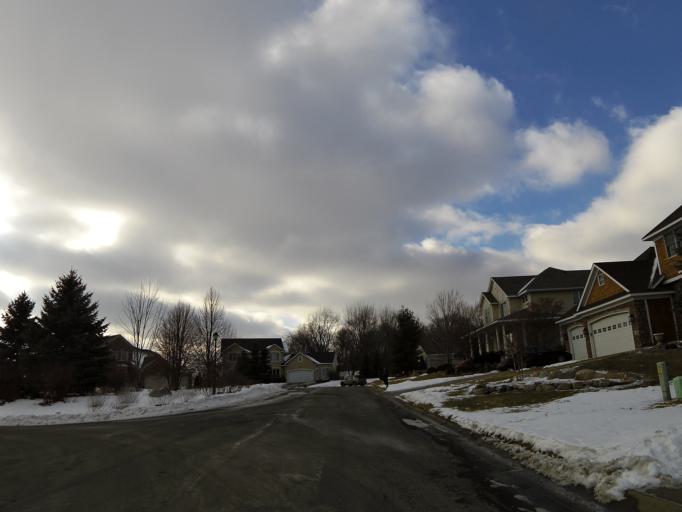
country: US
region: Minnesota
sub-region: Scott County
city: Prior Lake
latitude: 44.7316
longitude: -93.4554
